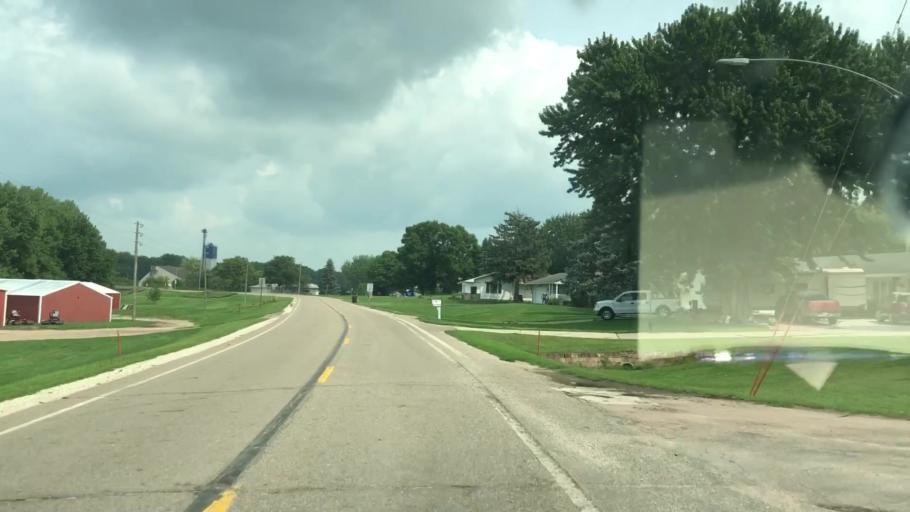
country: US
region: Iowa
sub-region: Plymouth County
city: Kingsley
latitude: 42.5835
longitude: -95.9699
